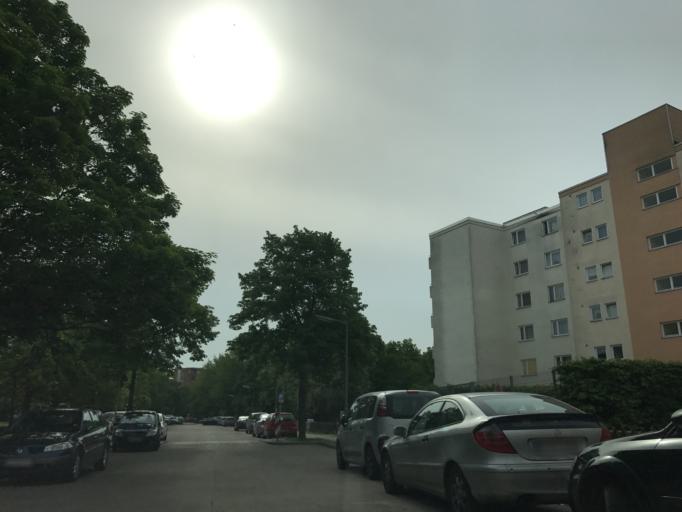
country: DE
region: Berlin
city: Staaken
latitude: 52.5309
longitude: 13.1464
